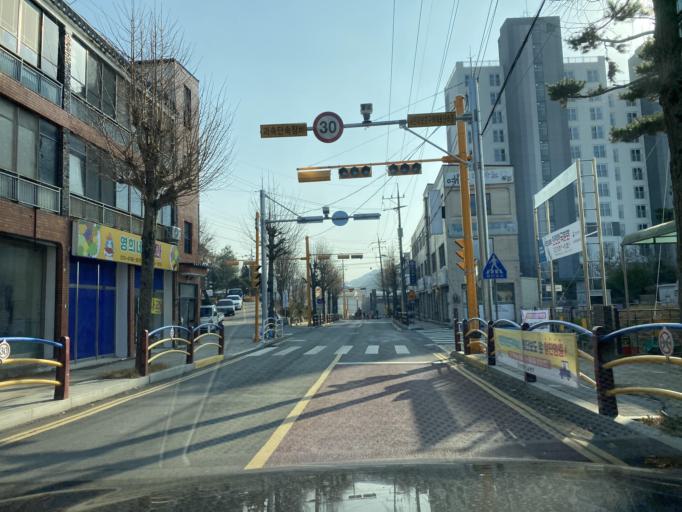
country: KR
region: Chungcheongnam-do
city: Yesan
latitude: 36.6837
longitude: 126.8325
